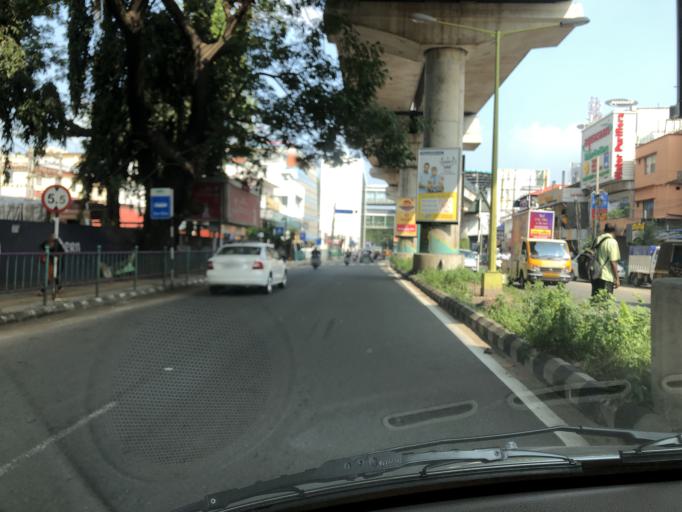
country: IN
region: Kerala
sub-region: Ernakulam
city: Elur
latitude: 10.0132
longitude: 76.3026
